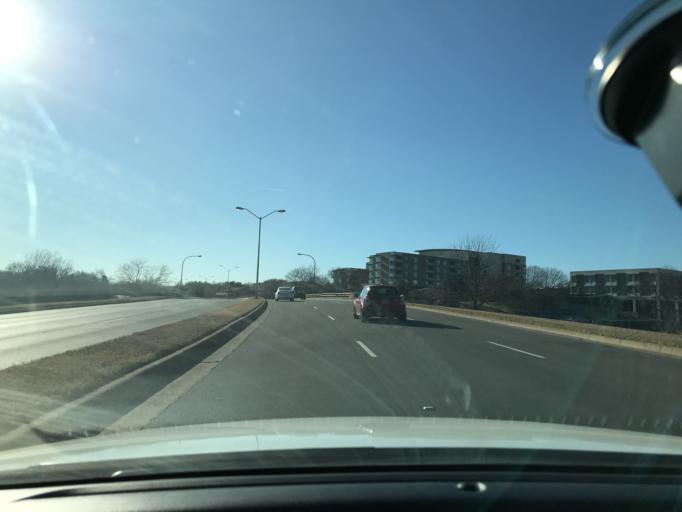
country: US
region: Texas
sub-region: Dallas County
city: Highland Park
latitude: 32.8527
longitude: -96.7278
